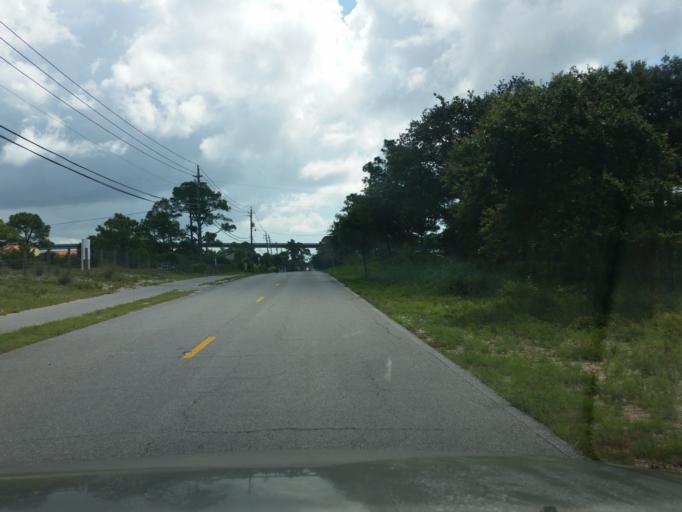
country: US
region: Alabama
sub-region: Baldwin County
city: Orange Beach
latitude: 30.3108
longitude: -87.4312
